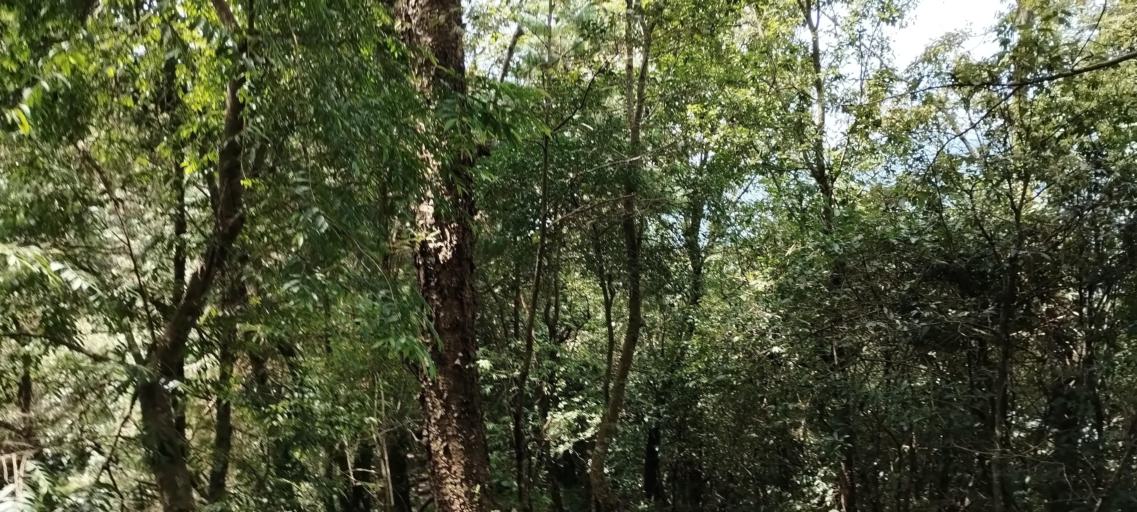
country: NP
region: Central Region
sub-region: Bagmati Zone
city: Kathmandu
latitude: 27.7877
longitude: 85.3766
